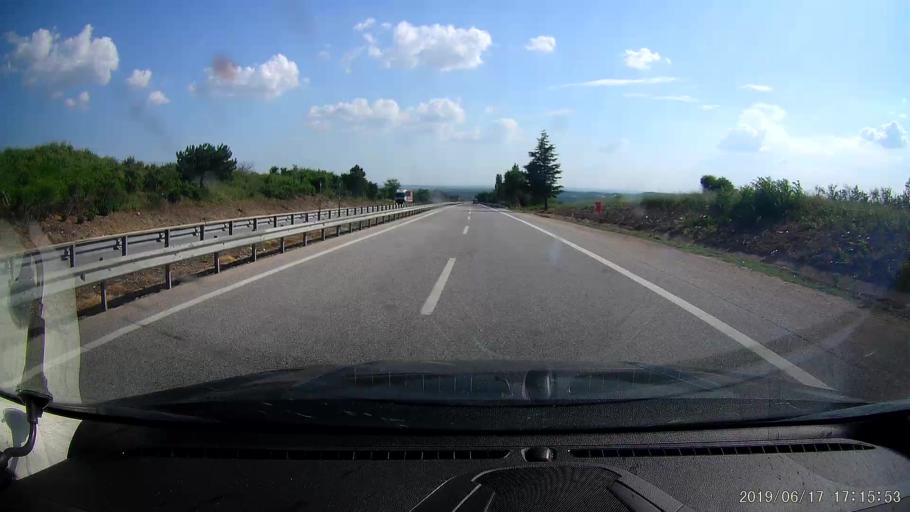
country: GR
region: East Macedonia and Thrace
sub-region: Nomos Evrou
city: Kastanies
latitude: 41.6997
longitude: 26.4878
